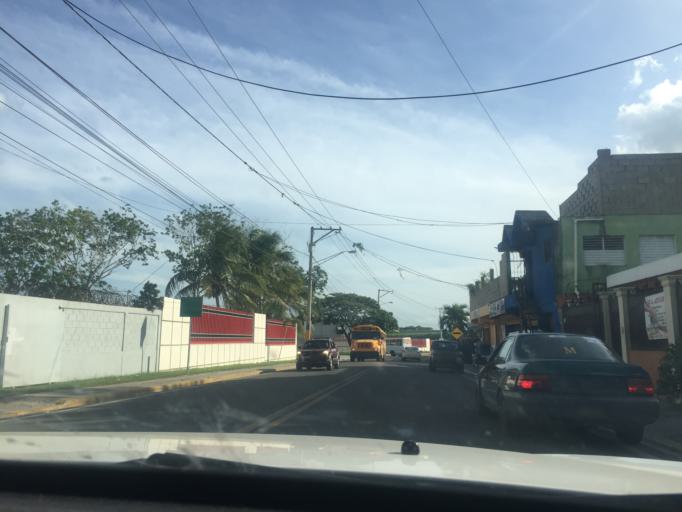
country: DO
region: Santiago
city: Tamboril
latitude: 19.4805
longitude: -70.6374
